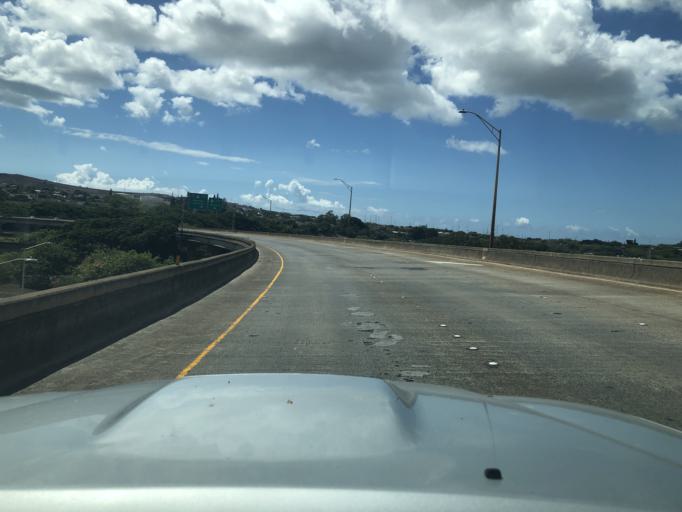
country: US
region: Hawaii
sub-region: Honolulu County
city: Halawa
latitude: 21.3730
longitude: -157.9271
